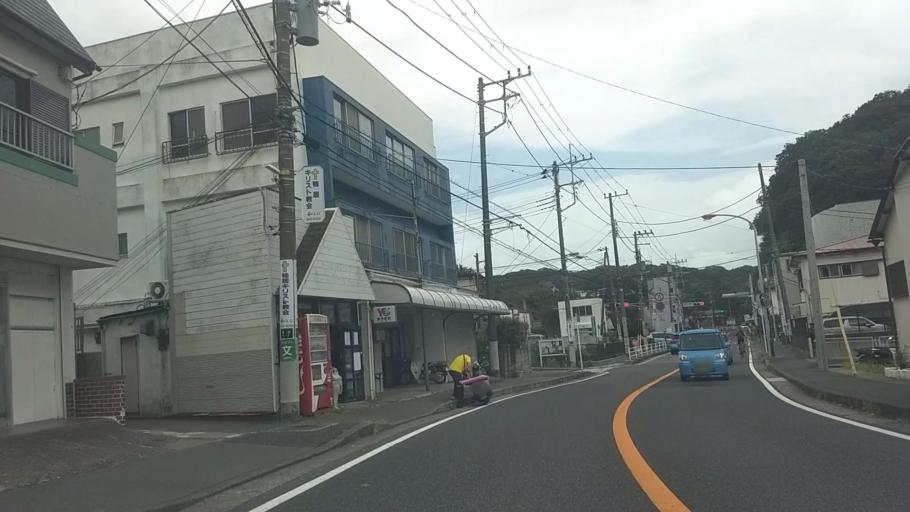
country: JP
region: Kanagawa
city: Yokosuka
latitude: 35.2499
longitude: 139.7302
